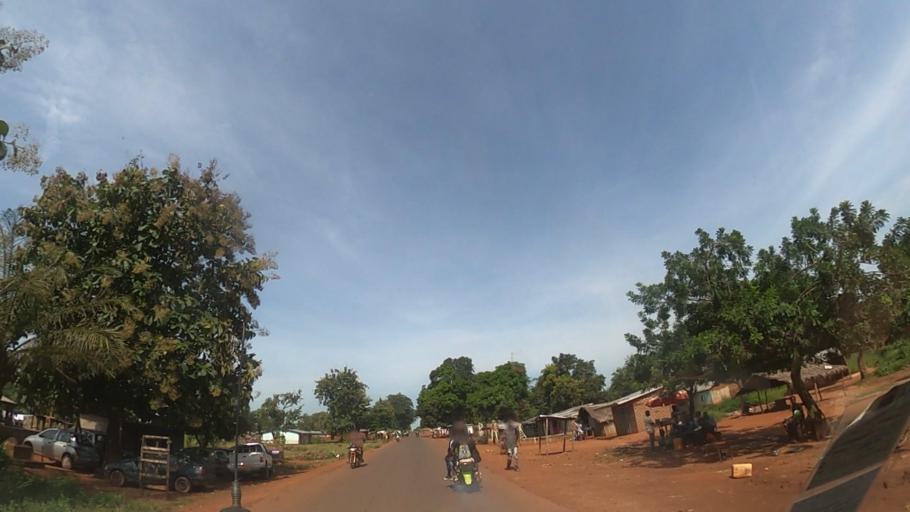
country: CF
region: Ombella-Mpoko
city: Bimbo
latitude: 4.3119
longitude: 18.4792
